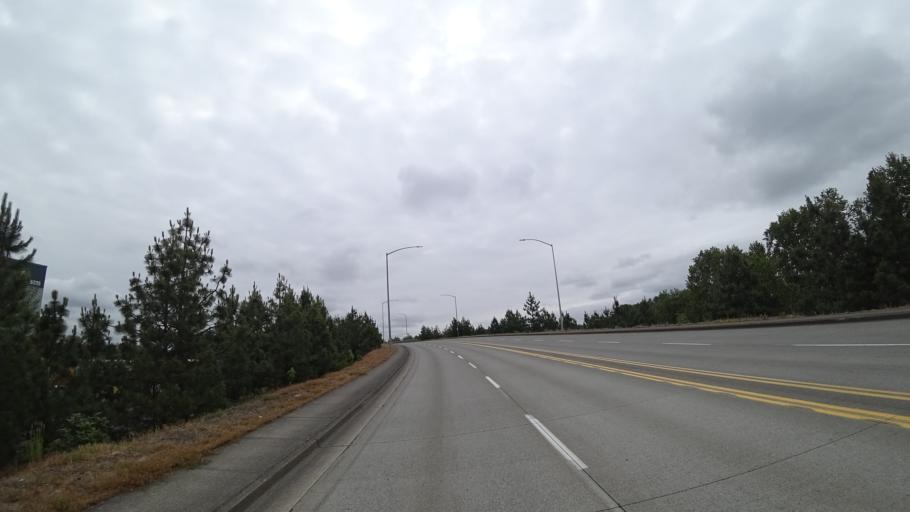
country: US
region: Washington
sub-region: Clark County
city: Vancouver
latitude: 45.6174
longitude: -122.7197
